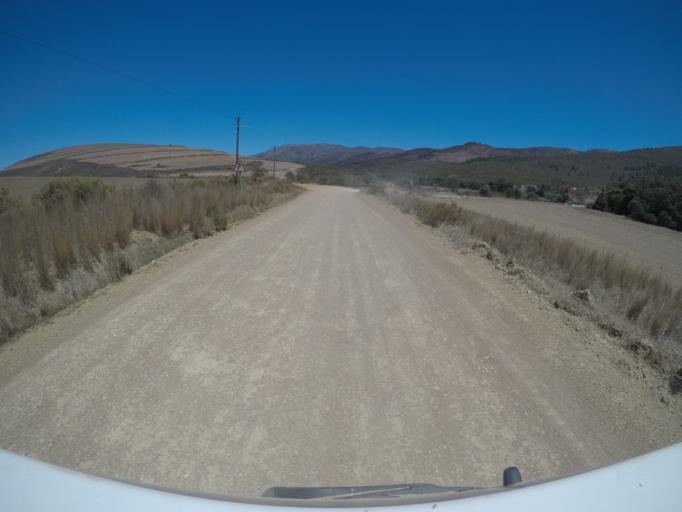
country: ZA
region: Western Cape
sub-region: Overberg District Municipality
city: Caledon
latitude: -34.1511
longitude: 19.2382
